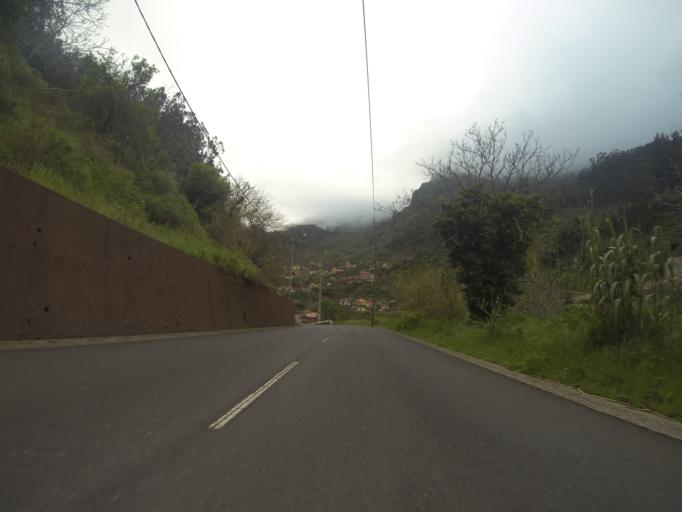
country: PT
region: Madeira
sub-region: Camara de Lobos
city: Curral das Freiras
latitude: 32.7320
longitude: -16.9682
